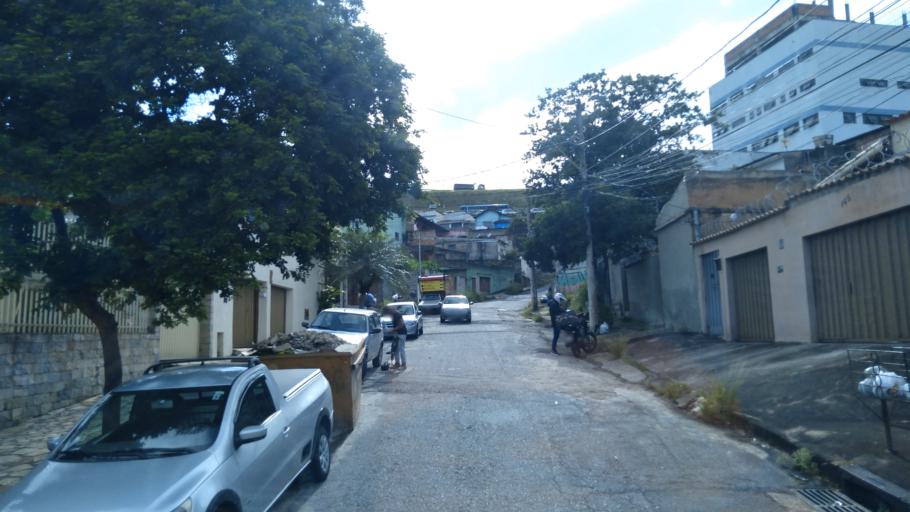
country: BR
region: Minas Gerais
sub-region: Belo Horizonte
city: Belo Horizonte
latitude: -19.9133
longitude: -43.9954
